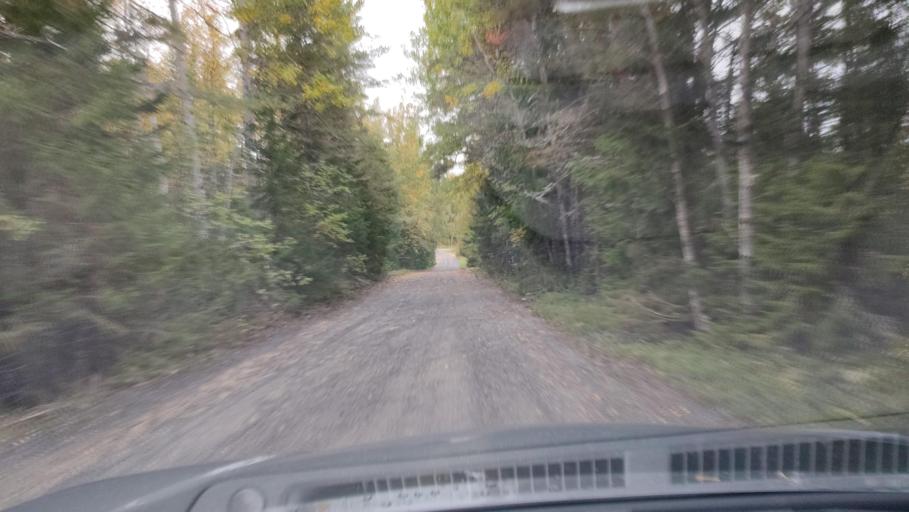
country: FI
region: Ostrobothnia
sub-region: Sydosterbotten
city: Kristinestad
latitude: 62.2758
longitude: 21.4034
